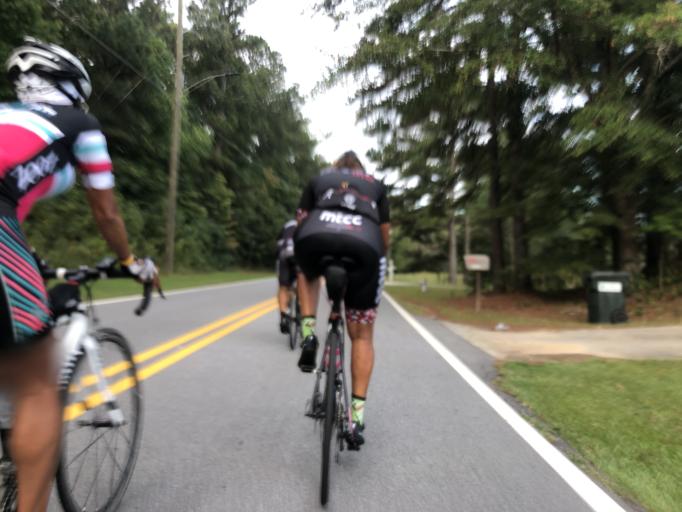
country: US
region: Georgia
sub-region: Fulton County
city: Fairburn
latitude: 33.6267
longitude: -84.6583
